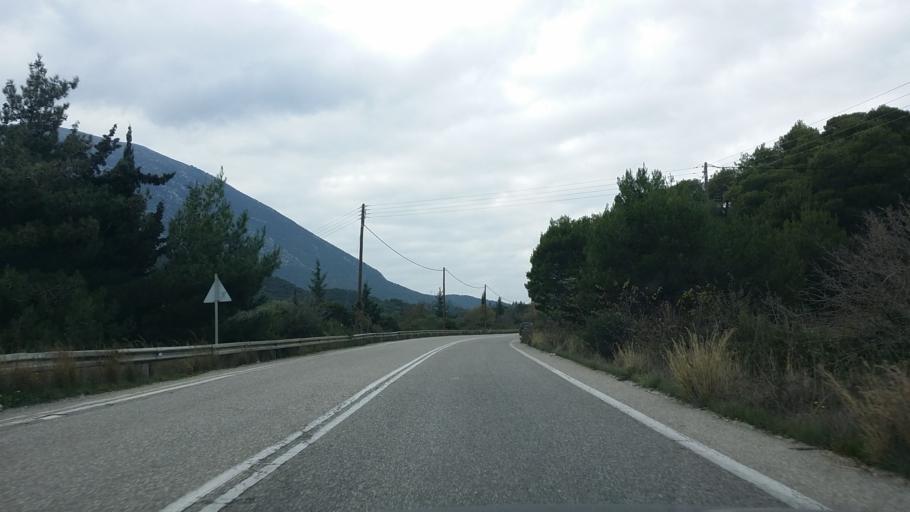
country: GR
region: West Greece
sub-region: Nomos Aitolias kai Akarnanias
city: Galatas
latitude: 38.3766
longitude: 21.6240
